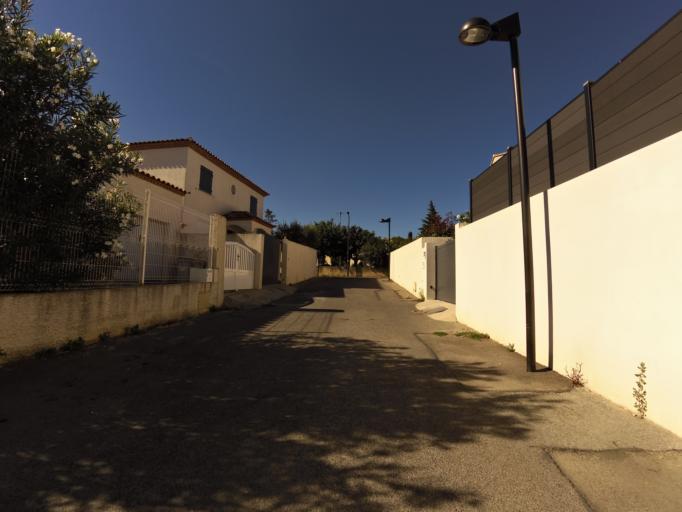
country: FR
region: Languedoc-Roussillon
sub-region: Departement du Gard
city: Aigues-Vives
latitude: 43.7242
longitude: 4.1786
